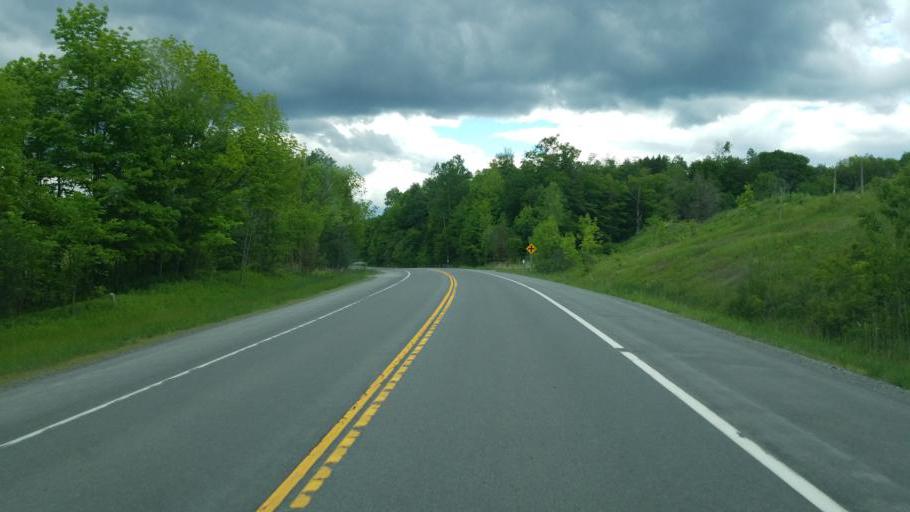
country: US
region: New York
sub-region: Oneida County
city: Chadwicks
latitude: 42.9690
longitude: -75.2521
